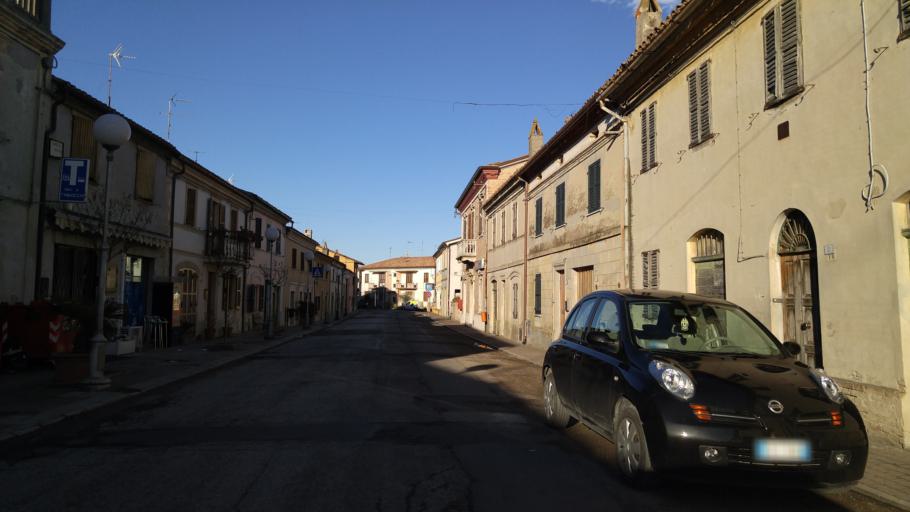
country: IT
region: The Marches
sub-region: Provincia di Pesaro e Urbino
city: Bellocchi
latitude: 43.7531
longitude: 13.0137
